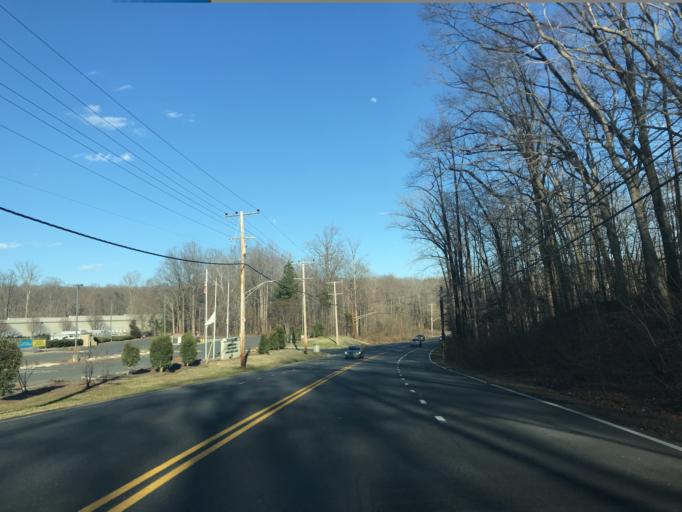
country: US
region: Maryland
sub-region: Anne Arundel County
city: Riva
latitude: 38.9277
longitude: -76.5938
